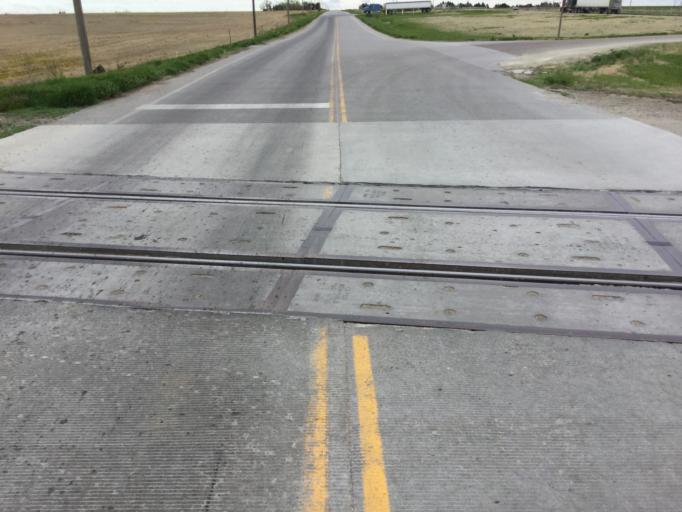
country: US
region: Kansas
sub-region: Phillips County
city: Phillipsburg
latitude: 39.7596
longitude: -99.3093
